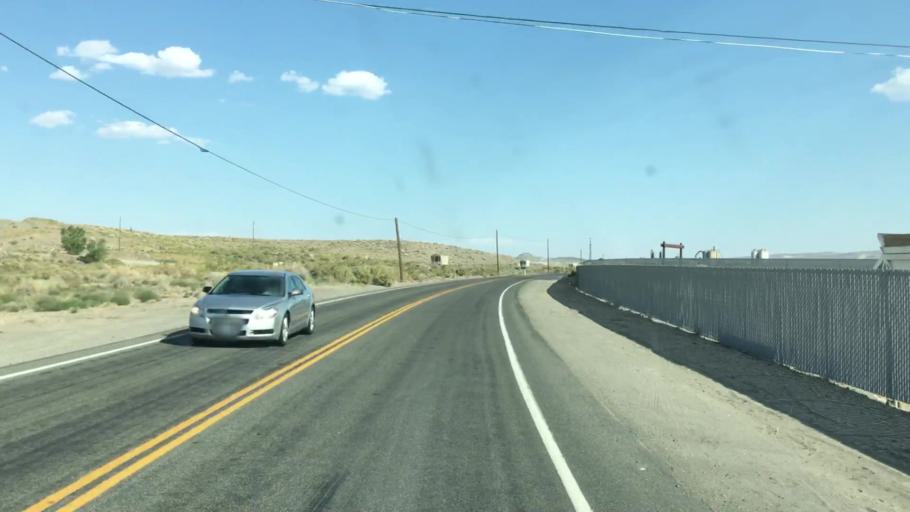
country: US
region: Nevada
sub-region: Lyon County
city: Fernley
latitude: 39.6301
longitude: -119.2775
